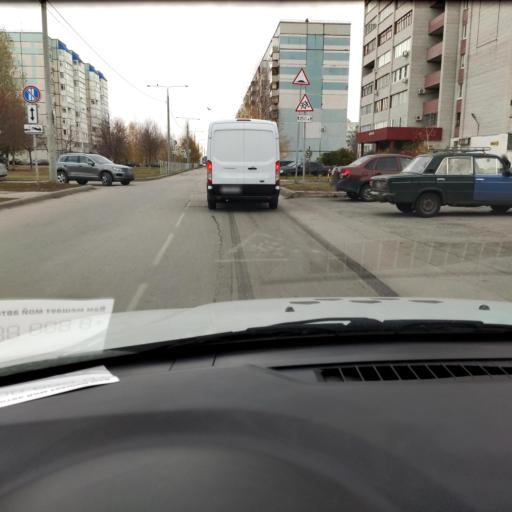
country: RU
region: Samara
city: Tol'yatti
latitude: 53.5437
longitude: 49.3543
